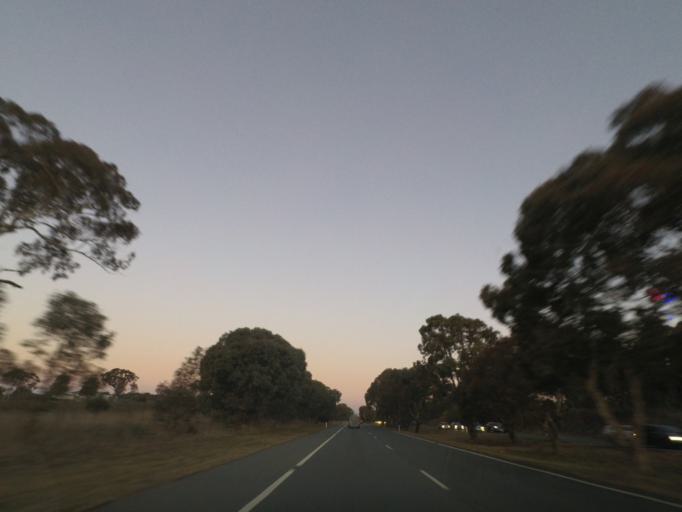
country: AU
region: Australian Capital Territory
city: Kaleen
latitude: -35.2071
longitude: 149.1039
